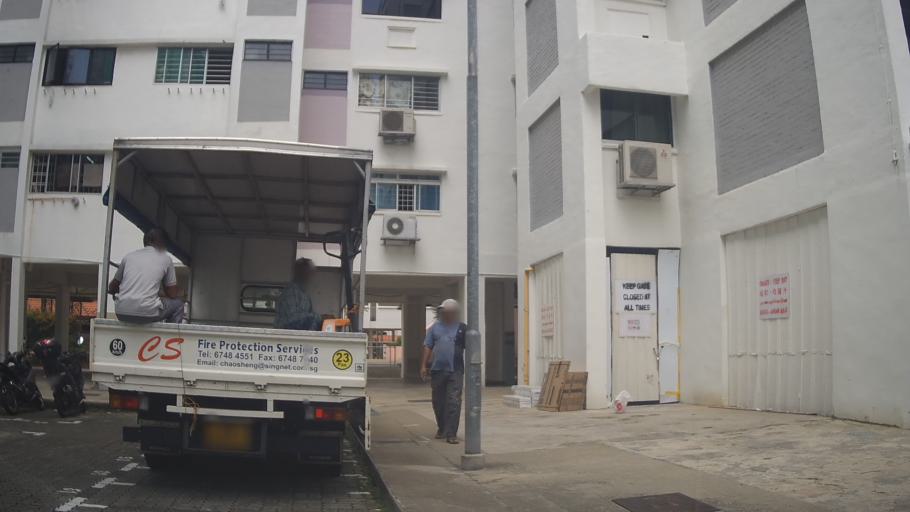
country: SG
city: Singapore
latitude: 1.3207
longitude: 103.8611
